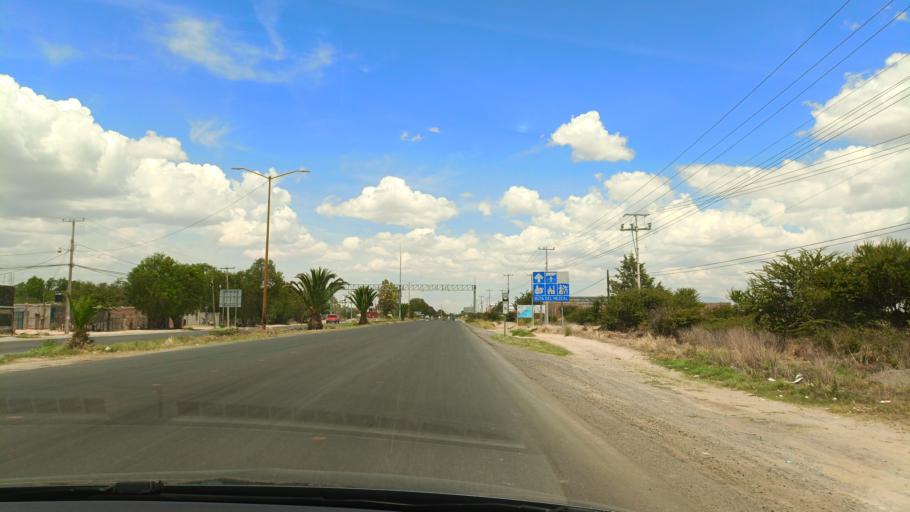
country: MX
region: Guanajuato
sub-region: San Luis de la Paz
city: San Ignacio
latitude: 21.2875
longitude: -100.5579
